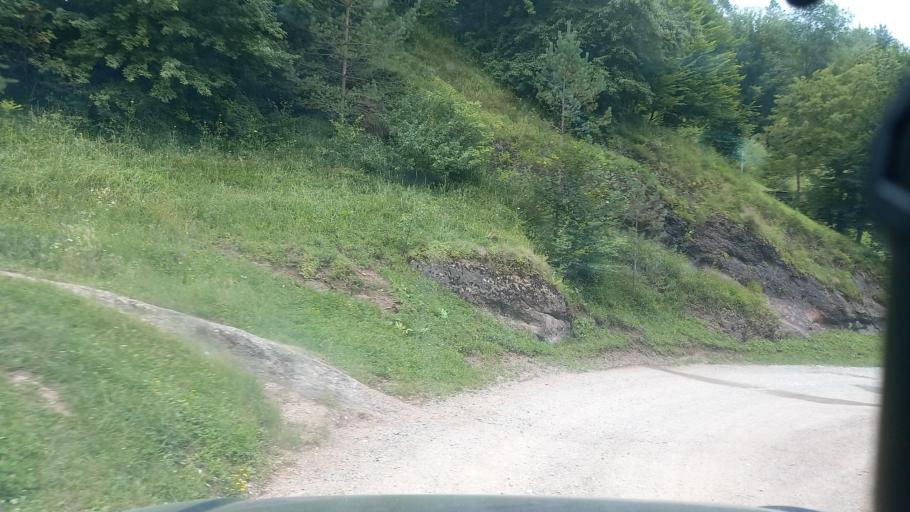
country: RU
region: Karachayevo-Cherkesiya
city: Kurdzhinovo
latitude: 43.8092
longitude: 40.9106
